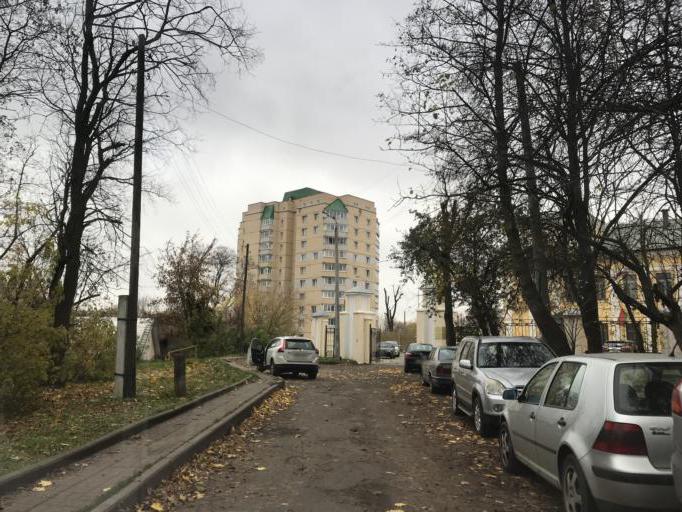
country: BY
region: Mogilev
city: Mahilyow
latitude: 53.9013
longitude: 30.3469
